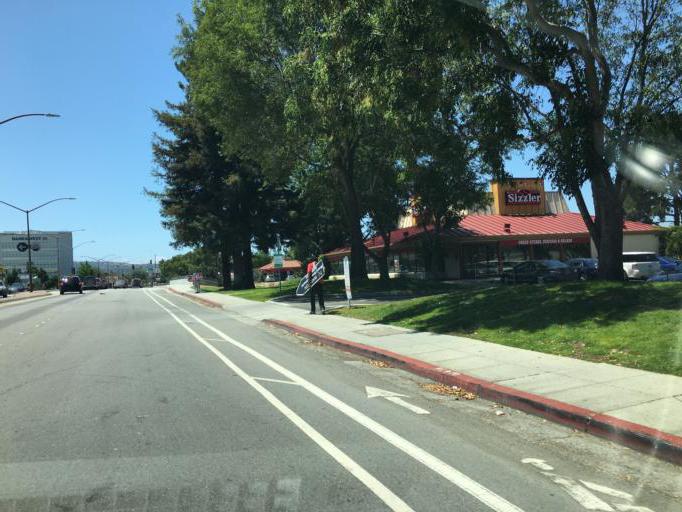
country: US
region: California
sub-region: San Mateo County
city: Redwood City
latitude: 37.4899
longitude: -122.2247
